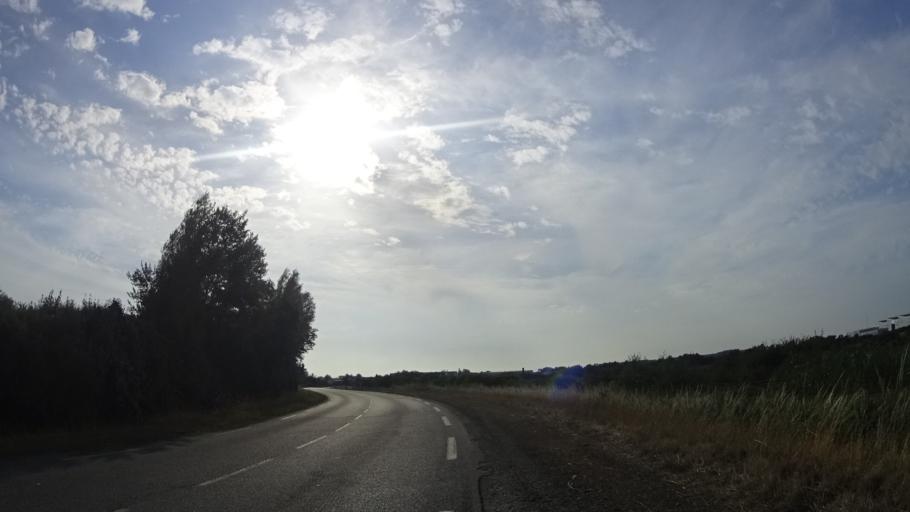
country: FR
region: Pays de la Loire
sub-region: Departement de la Loire-Atlantique
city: Trignac
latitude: 47.3059
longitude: -2.1680
